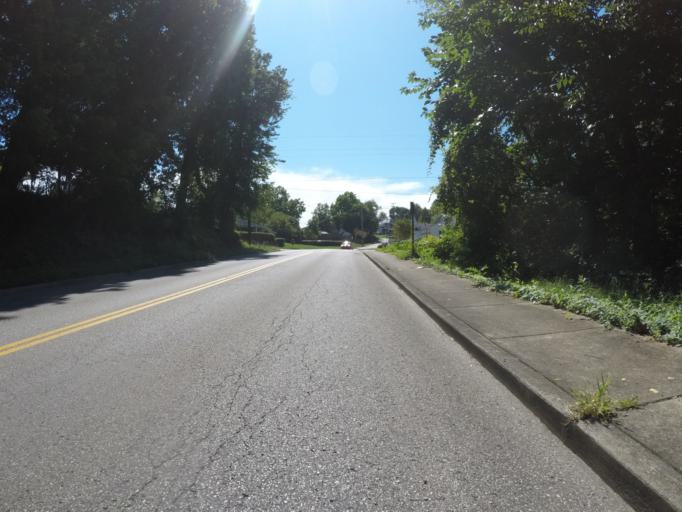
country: US
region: Kentucky
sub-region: Boyd County
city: Ashland
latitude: 38.4590
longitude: -82.6494
